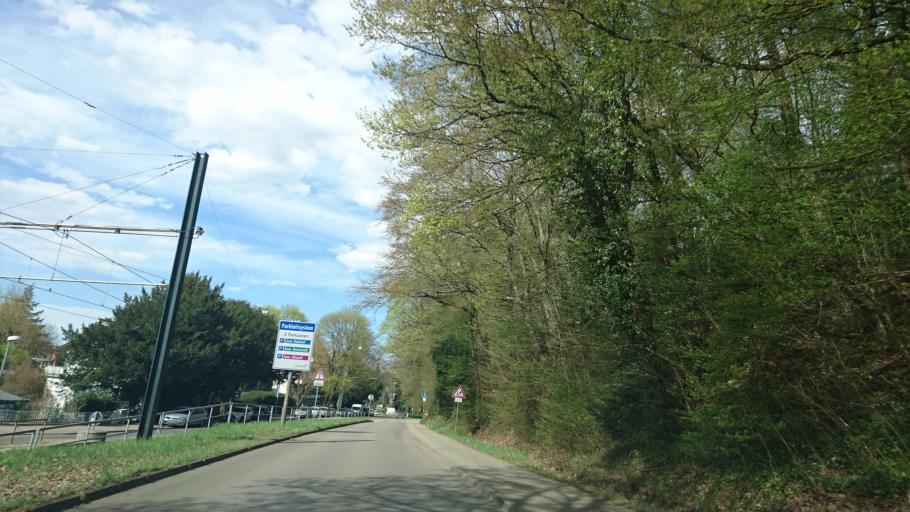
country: DE
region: Baden-Wuerttemberg
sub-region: Freiburg Region
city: Freiburg
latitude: 47.9796
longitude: 7.8481
